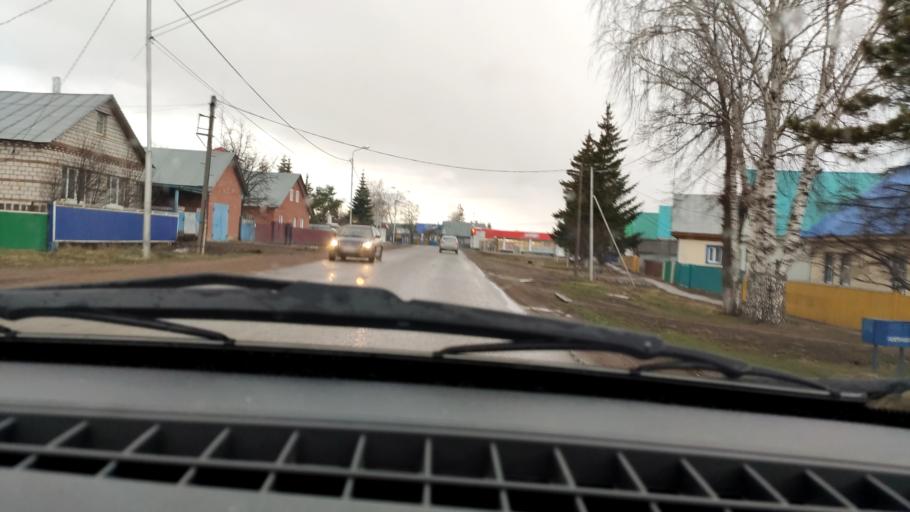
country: RU
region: Bashkortostan
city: Chekmagush
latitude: 55.1331
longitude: 54.6568
